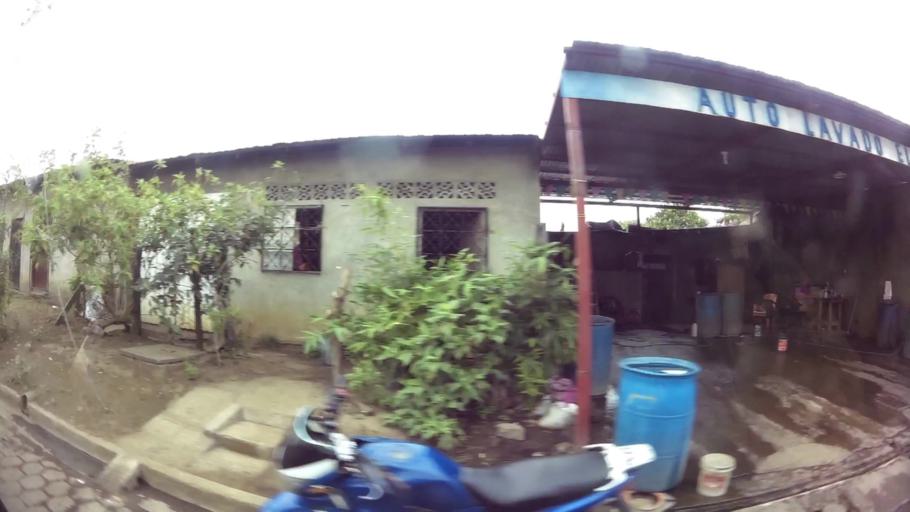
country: NI
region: Leon
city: Leon
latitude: 12.4454
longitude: -86.8674
